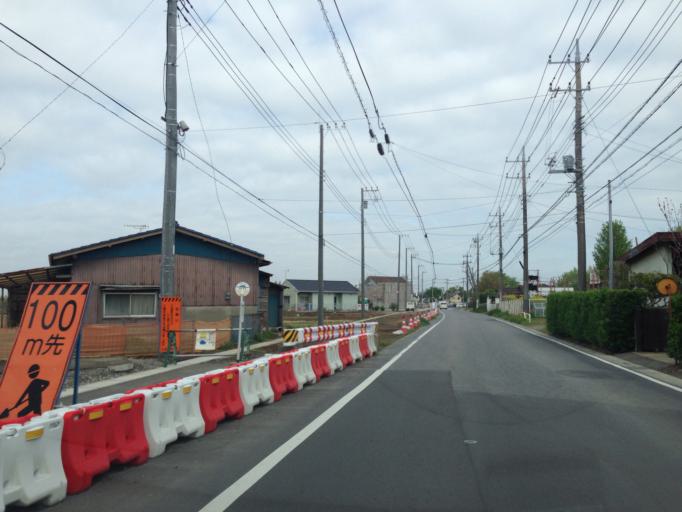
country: JP
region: Ibaraki
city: Ishige
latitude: 36.1392
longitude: 140.0447
